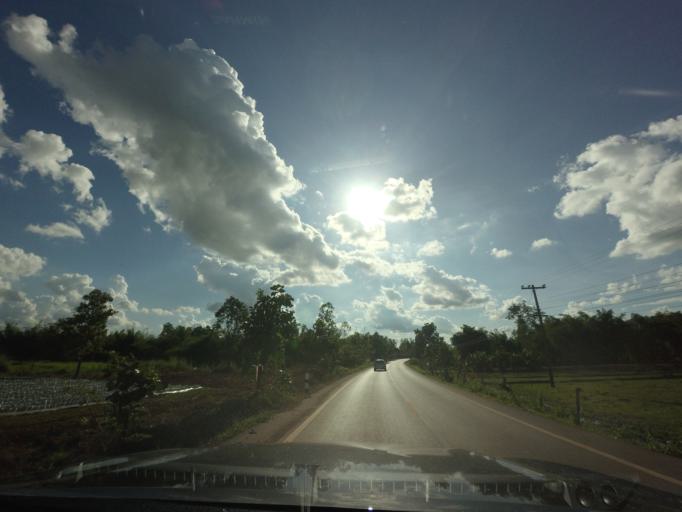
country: TH
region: Changwat Udon Thani
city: Ban Dung
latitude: 17.7429
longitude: 103.3125
